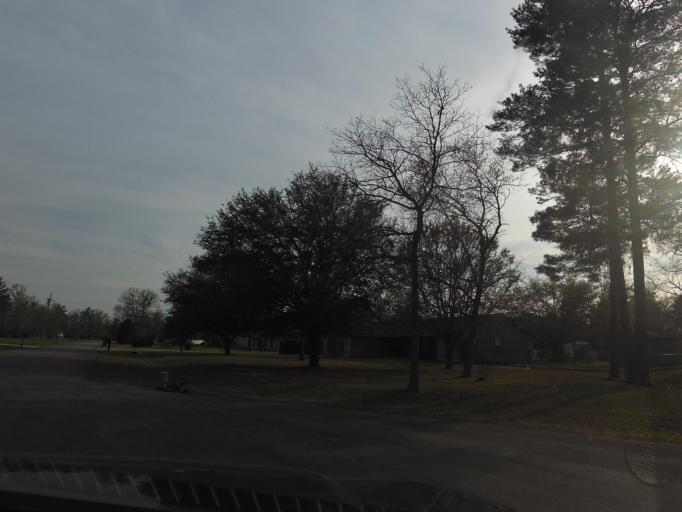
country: US
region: Florida
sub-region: Clay County
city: Middleburg
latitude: 30.1169
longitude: -81.8871
